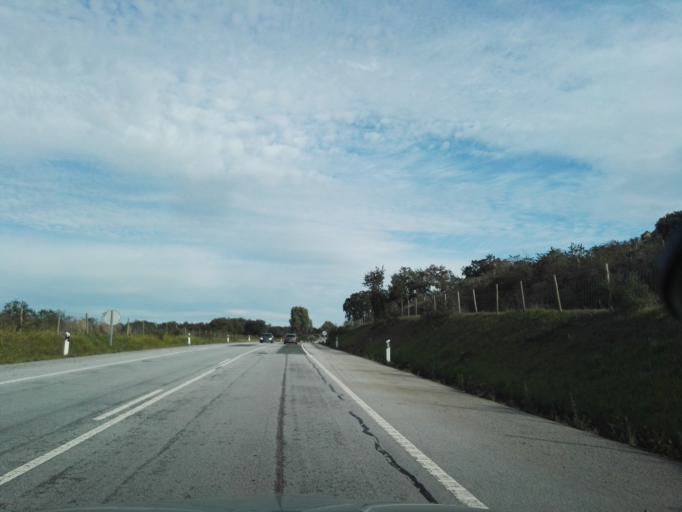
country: PT
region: Portalegre
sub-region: Nisa
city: Nisa
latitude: 39.4307
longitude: -7.7169
